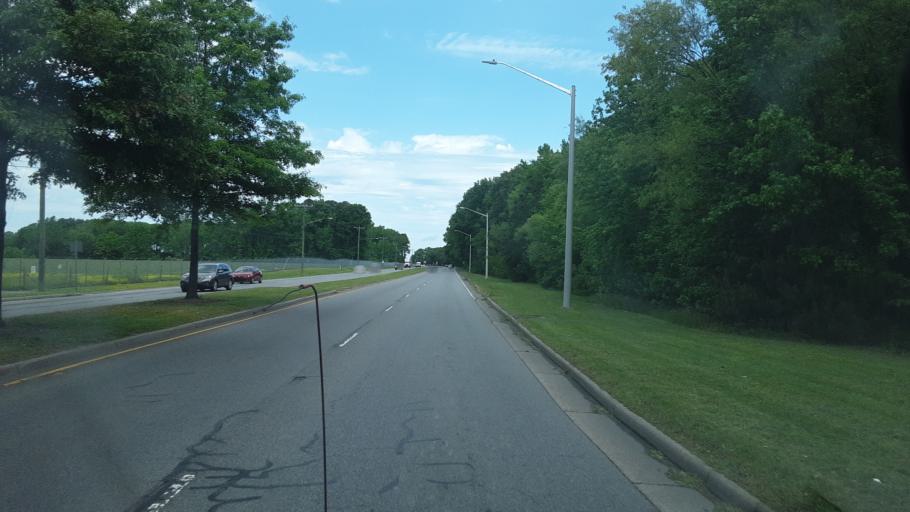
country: US
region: Virginia
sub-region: City of Virginia Beach
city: Virginia Beach
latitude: 36.8036
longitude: -76.0048
